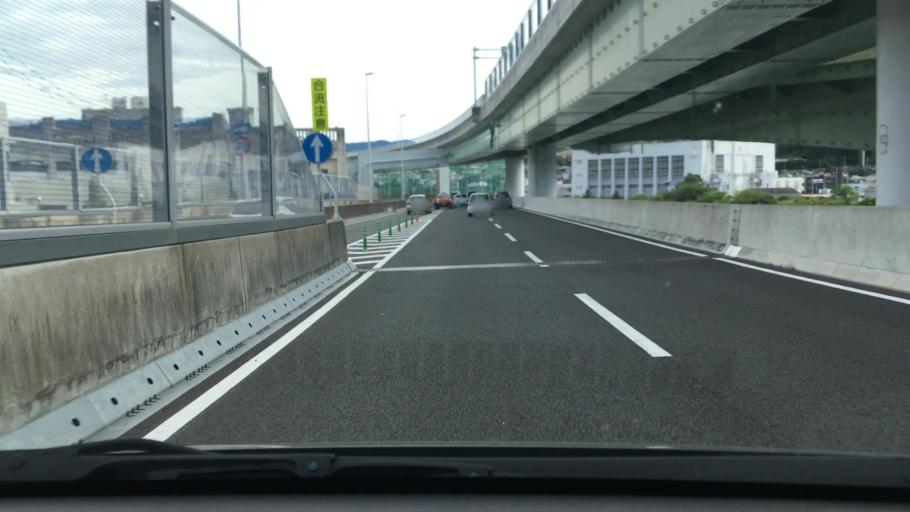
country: JP
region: Nagasaki
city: Nagasaki-shi
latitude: 32.7625
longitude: 129.8619
